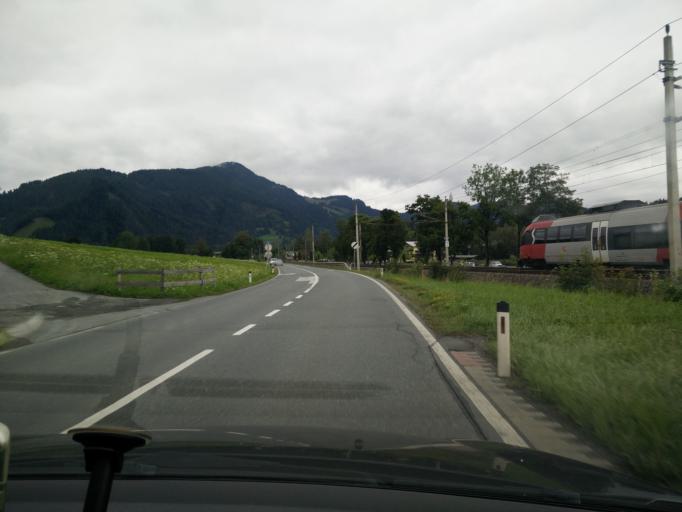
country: AT
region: Tyrol
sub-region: Politischer Bezirk Kitzbuhel
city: Reith bei Kitzbuhel
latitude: 47.4547
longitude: 12.3669
